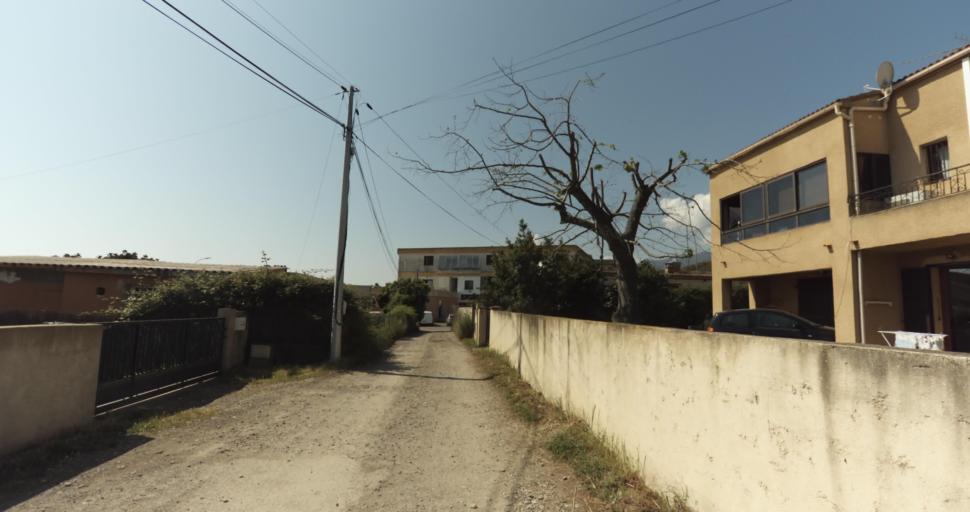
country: FR
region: Corsica
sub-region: Departement de la Haute-Corse
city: Biguglia
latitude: 42.6289
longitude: 9.4307
